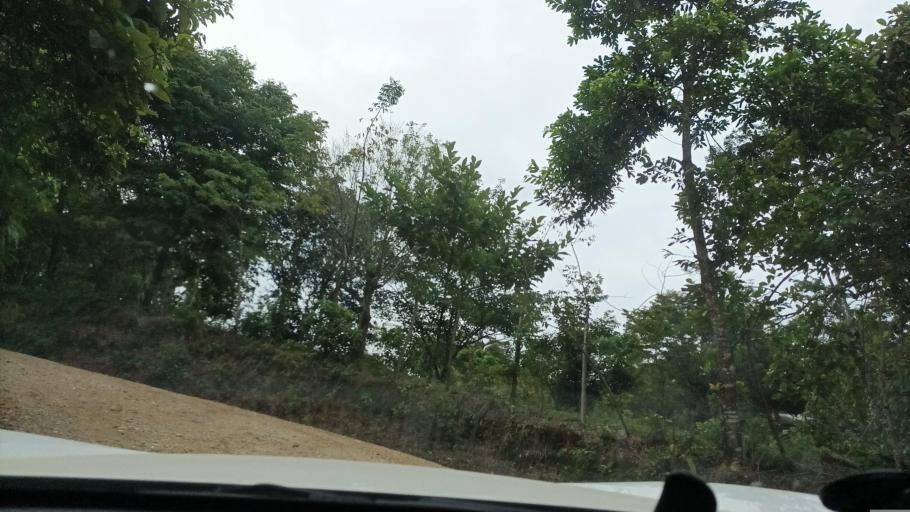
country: MX
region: Veracruz
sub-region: Uxpanapa
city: Poblado 10
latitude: 17.5732
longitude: -94.4230
